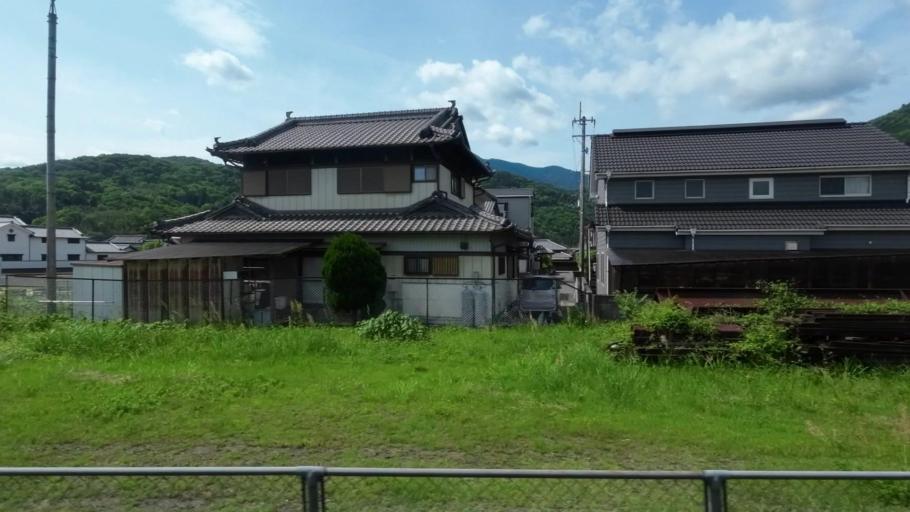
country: JP
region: Tokushima
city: Wakimachi
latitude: 34.0611
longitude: 134.2052
